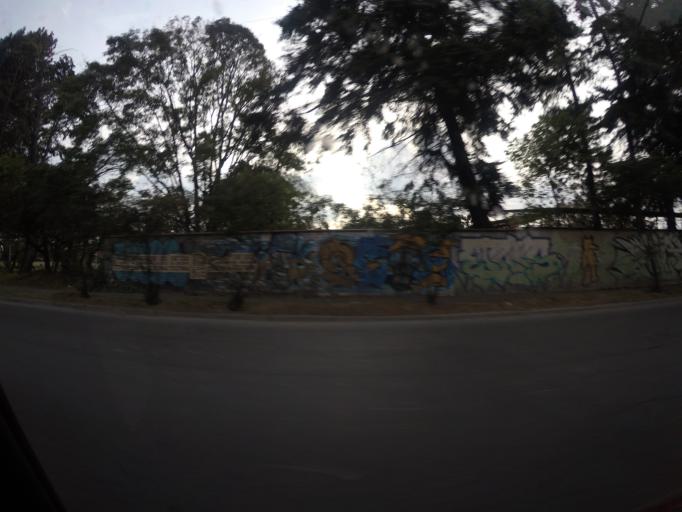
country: CO
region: Bogota D.C.
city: Barrio San Luis
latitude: 4.7043
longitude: -74.0815
